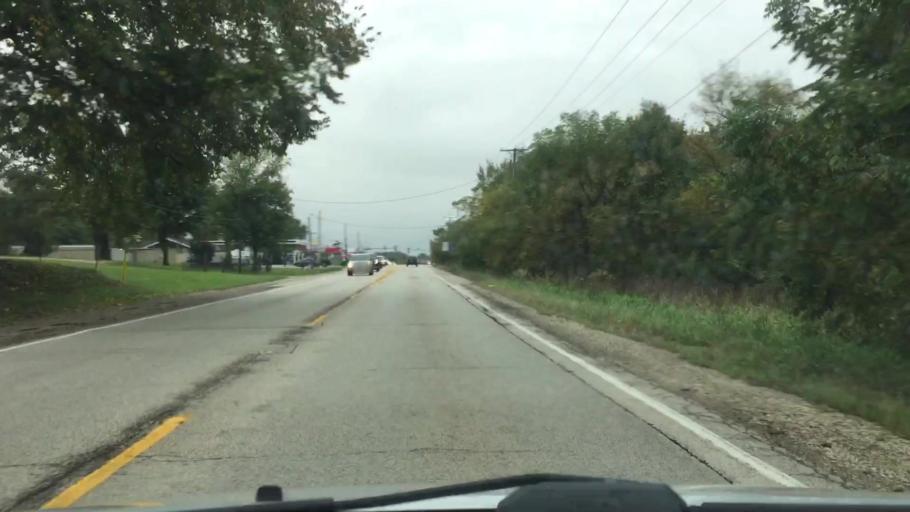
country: US
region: Illinois
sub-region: McHenry County
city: Richmond
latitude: 42.4538
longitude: -88.3059
